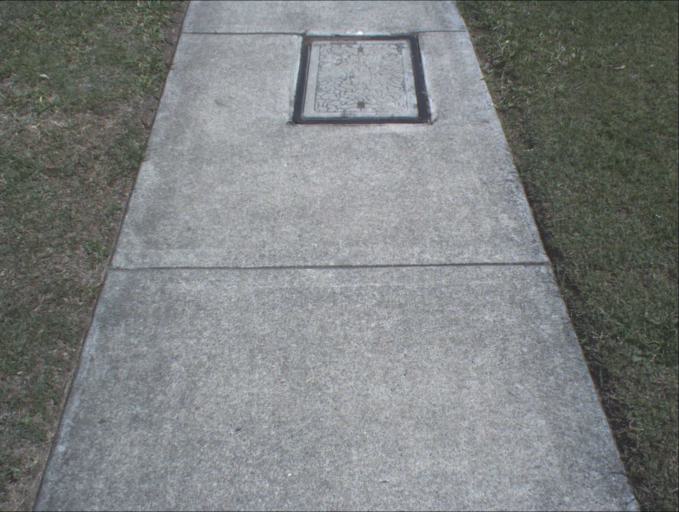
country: AU
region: Queensland
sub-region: Logan
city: Park Ridge South
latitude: -27.6654
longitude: 153.0251
